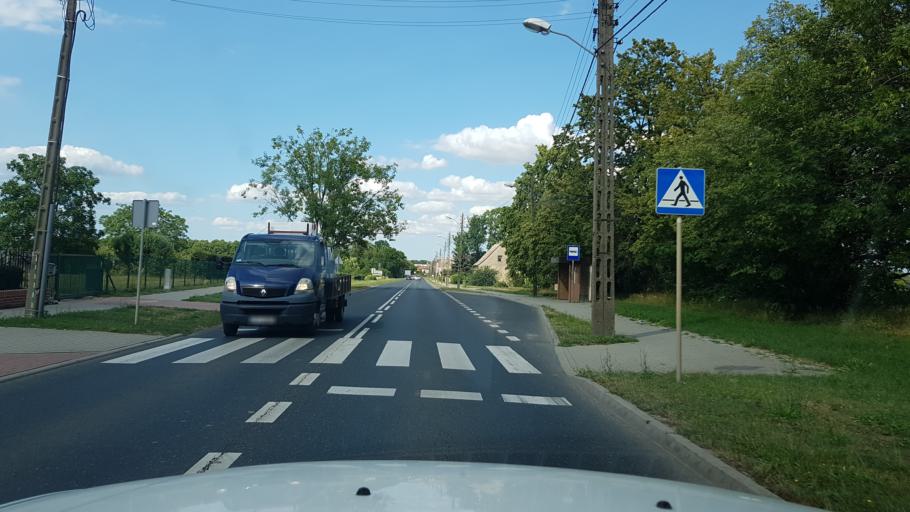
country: PL
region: West Pomeranian Voivodeship
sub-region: Powiat pyrzycki
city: Pyrzyce
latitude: 53.1296
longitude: 14.8896
